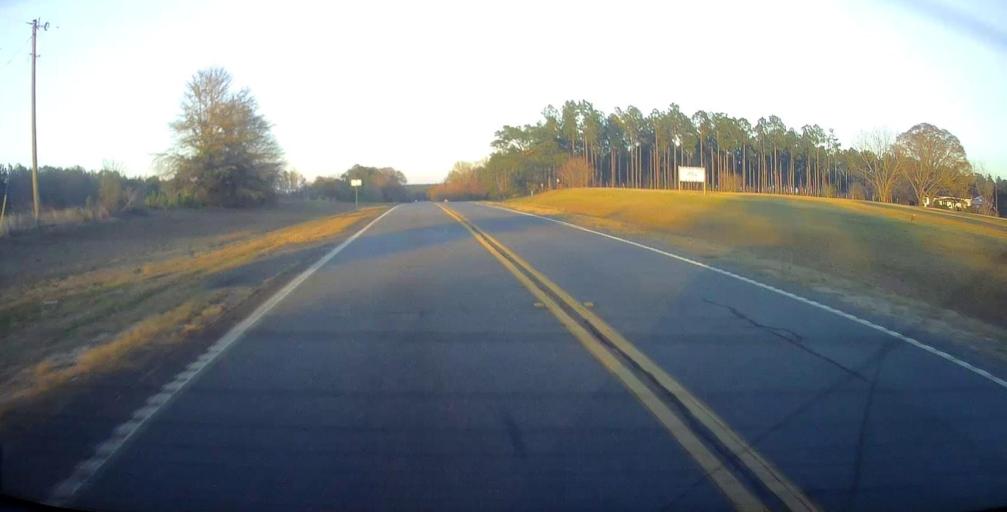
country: US
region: Georgia
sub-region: Dodge County
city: Chester
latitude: 32.2960
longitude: -83.0850
